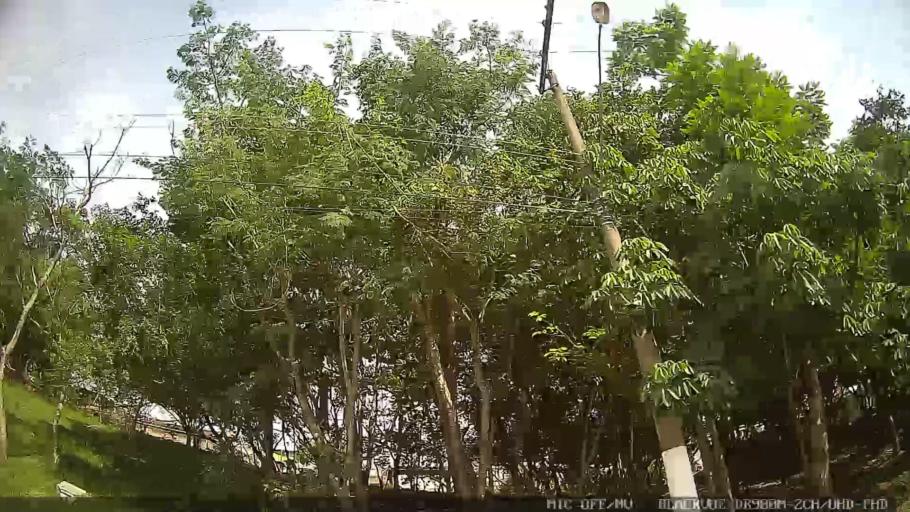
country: BR
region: Sao Paulo
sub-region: Braganca Paulista
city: Braganca Paulista
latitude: -22.9139
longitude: -46.5452
